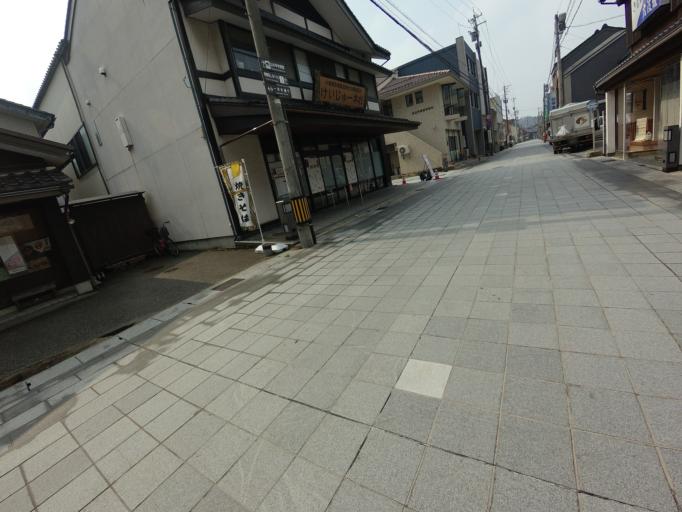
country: JP
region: Ishikawa
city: Nanao
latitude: 37.0474
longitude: 136.9625
